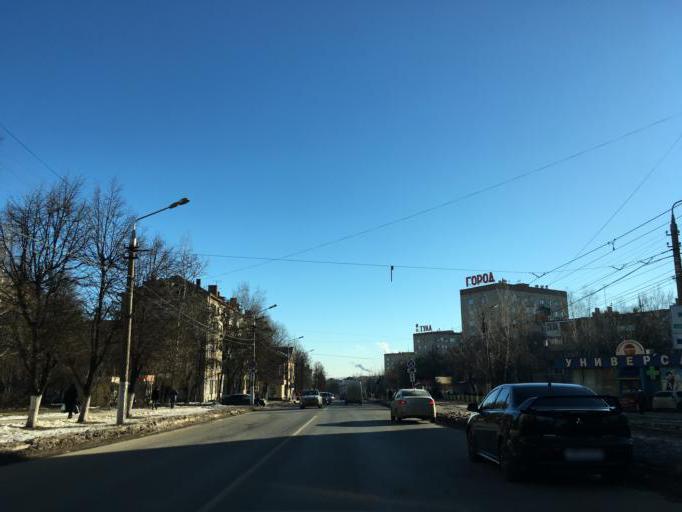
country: RU
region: Tula
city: Tula
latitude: 54.1904
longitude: 37.6893
